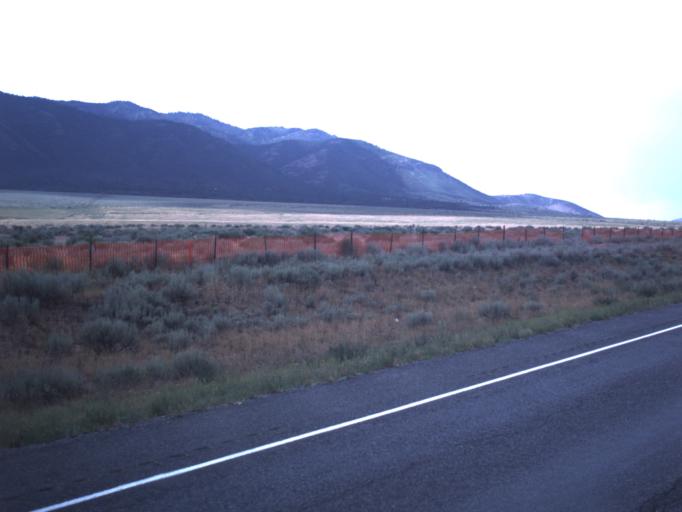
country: US
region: Utah
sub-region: Sanpete County
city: Fountain Green
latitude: 39.6810
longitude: -111.6729
